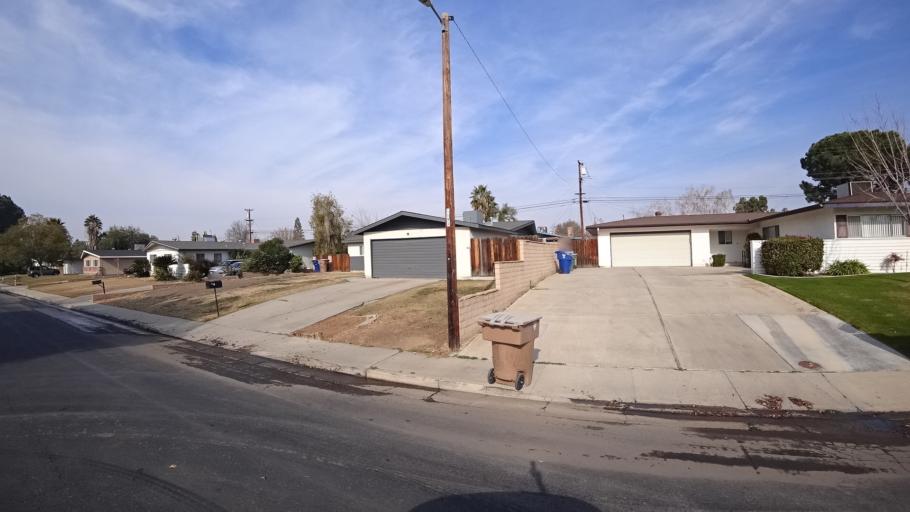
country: US
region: California
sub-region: Kern County
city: Oildale
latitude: 35.3998
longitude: -118.9644
